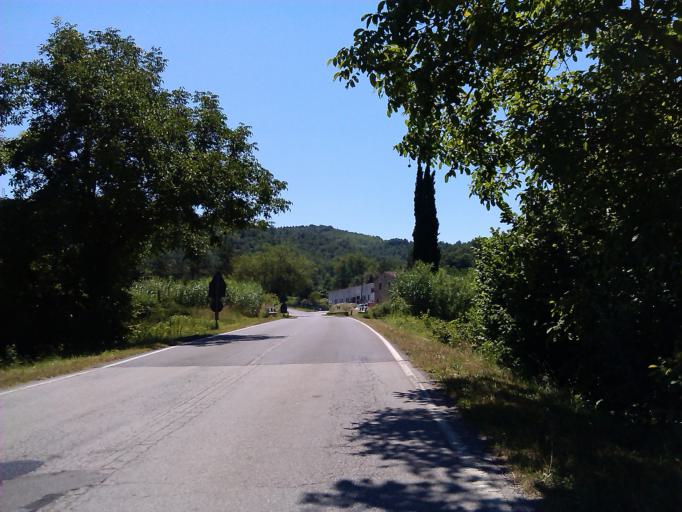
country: IT
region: Umbria
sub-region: Provincia di Terni
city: Fabro Scalo
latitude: 42.8658
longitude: 12.0489
